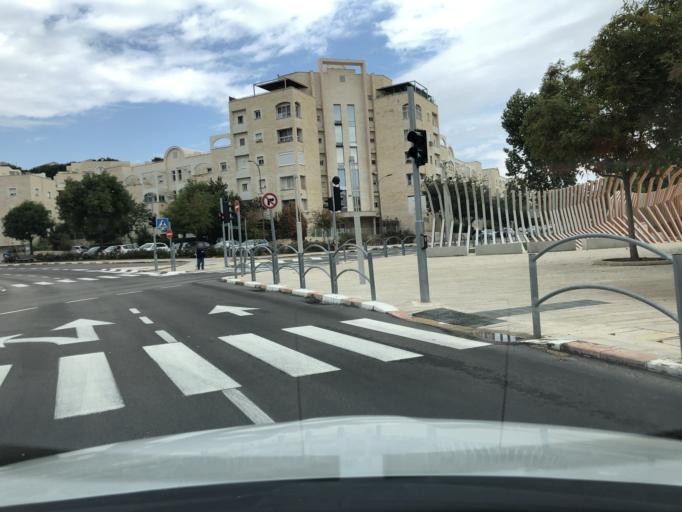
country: IL
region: Central District
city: Modiin
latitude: 31.9022
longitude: 35.0096
